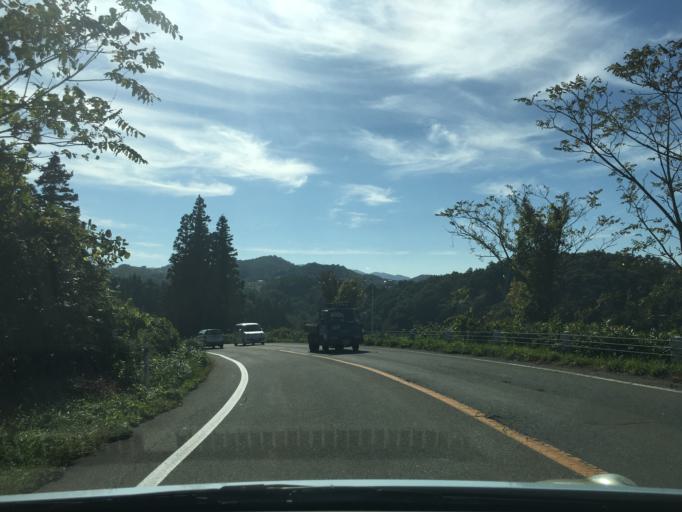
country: JP
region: Fukushima
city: Kitakata
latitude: 37.5356
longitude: 139.9594
